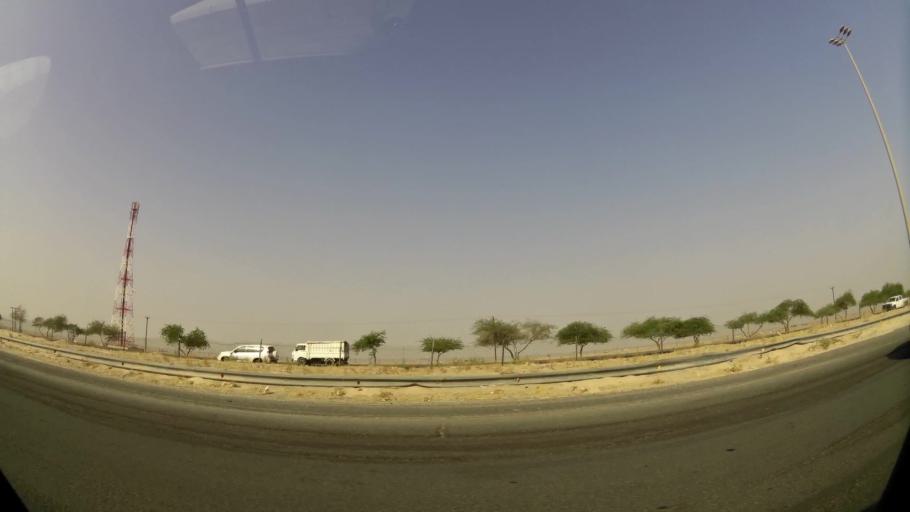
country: KW
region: Al Asimah
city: Ar Rabiyah
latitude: 29.1986
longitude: 47.8820
